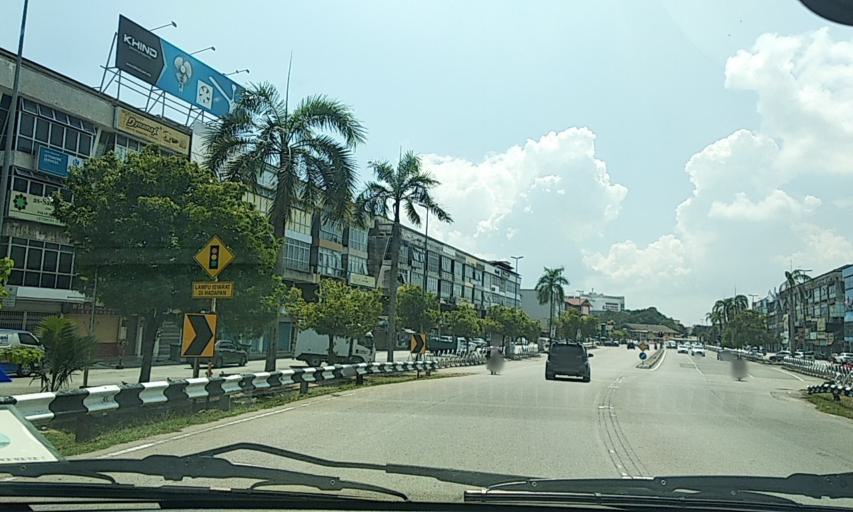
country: MY
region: Kedah
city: Sungai Petani
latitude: 5.6393
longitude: 100.4827
